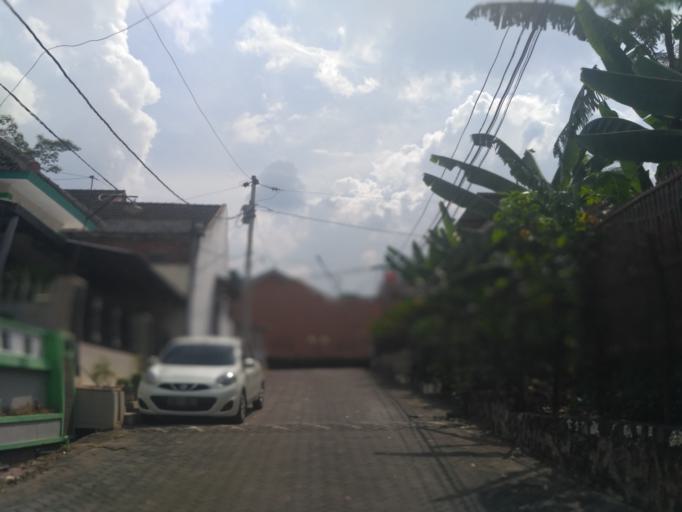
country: ID
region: Central Java
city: Ungaran
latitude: -7.0732
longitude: 110.4408
